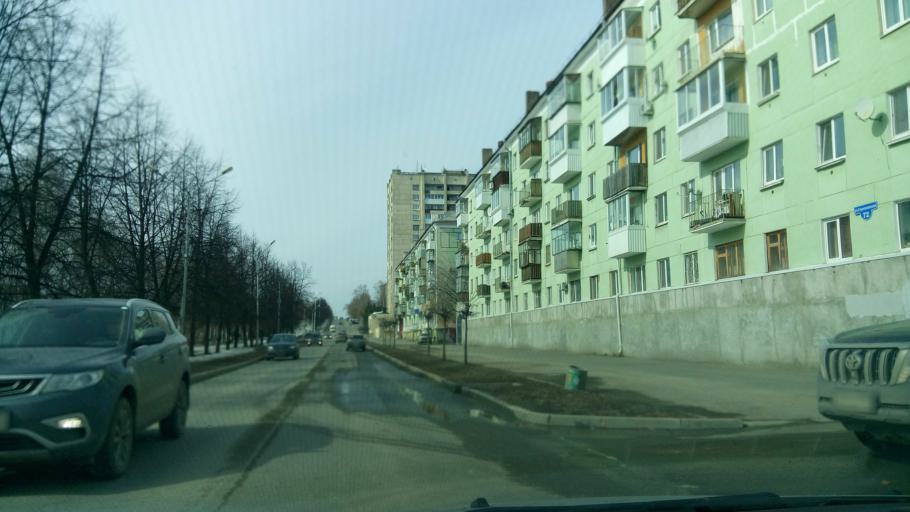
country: RU
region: Sverdlovsk
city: Nizhniy Tagil
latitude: 57.9056
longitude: 59.9771
